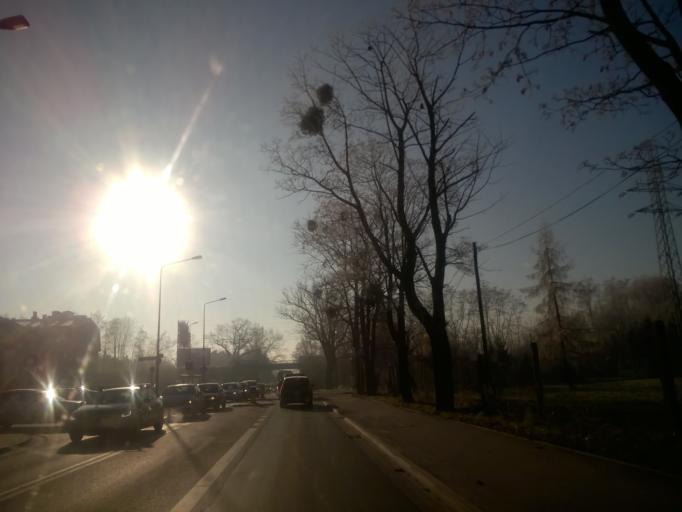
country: PL
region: Lower Silesian Voivodeship
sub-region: Powiat wroclawski
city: Wroclaw
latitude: 51.0721
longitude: 17.0325
